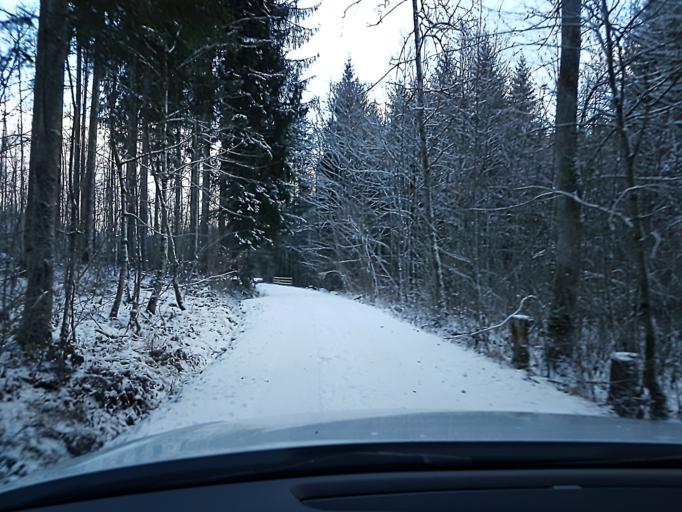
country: DE
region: Baden-Wuerttemberg
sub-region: Regierungsbezirk Stuttgart
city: Fichtenberg
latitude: 48.9731
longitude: 9.7096
